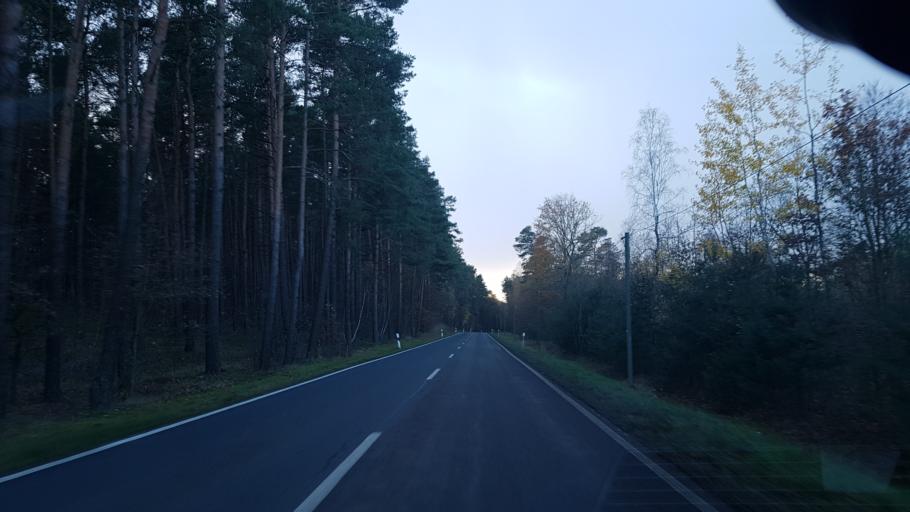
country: DE
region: Brandenburg
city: Sonnewalde
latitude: 51.7247
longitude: 13.6928
